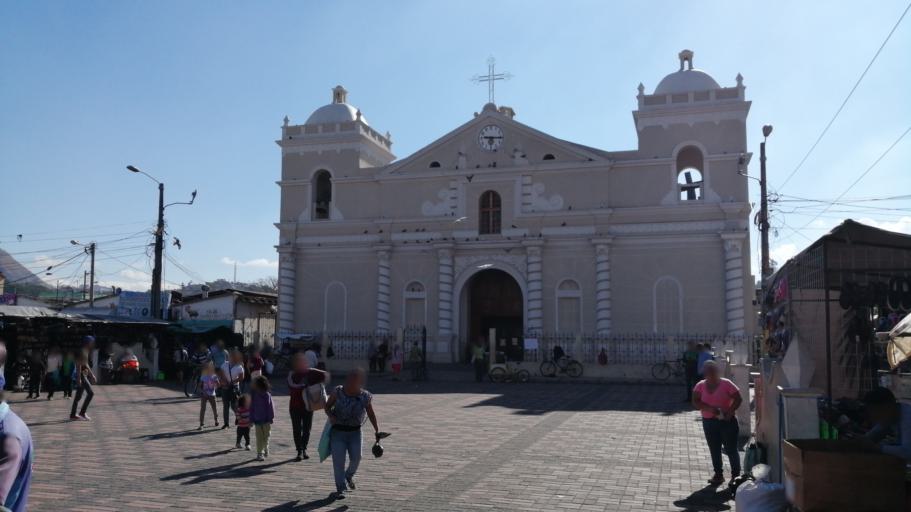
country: GT
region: Guatemala
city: Amatitlan
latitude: 14.4789
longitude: -90.6192
